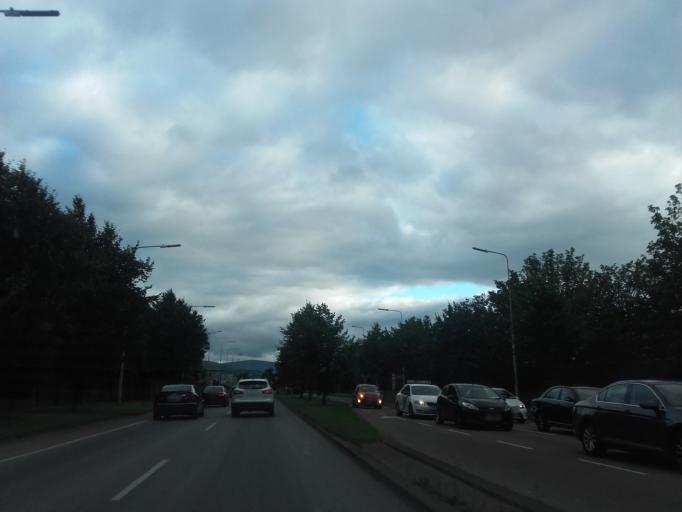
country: IE
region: Leinster
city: Tallaght
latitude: 53.2927
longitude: -6.3688
